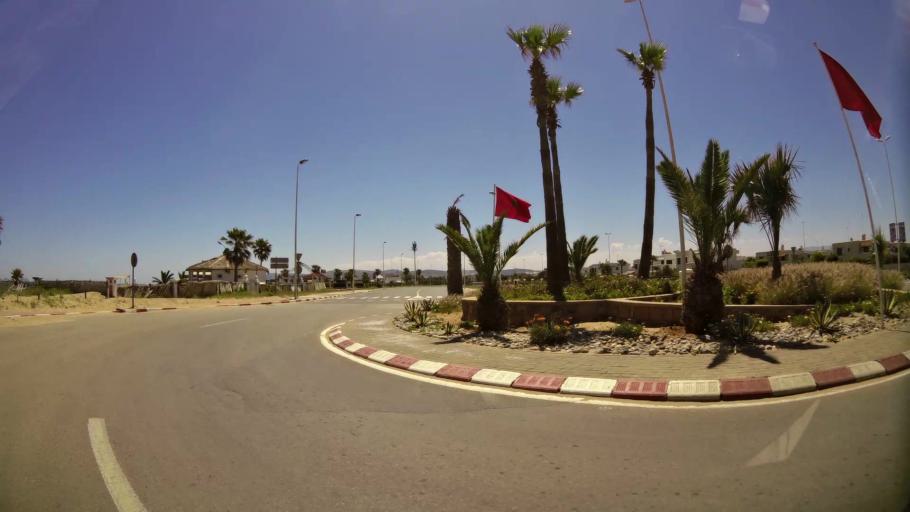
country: MA
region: Oriental
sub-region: Berkane-Taourirt
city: Madagh
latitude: 35.0974
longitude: -2.2646
